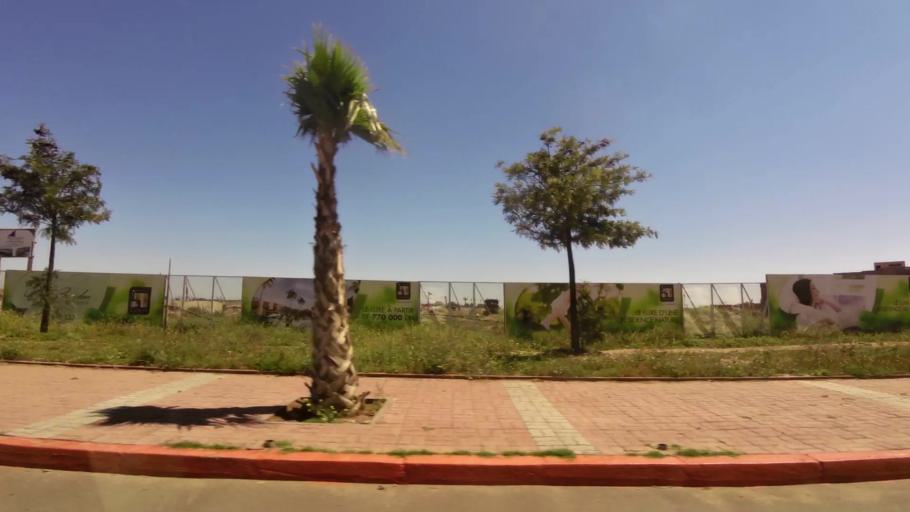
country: MA
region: Marrakech-Tensift-Al Haouz
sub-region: Marrakech
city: Marrakesh
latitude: 31.6008
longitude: -7.9968
